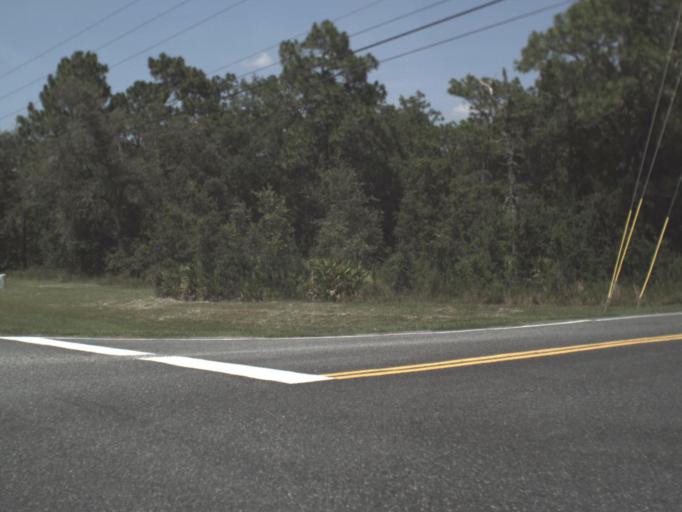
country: US
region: Florida
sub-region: Citrus County
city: Sugarmill Woods
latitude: 28.7088
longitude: -82.5525
